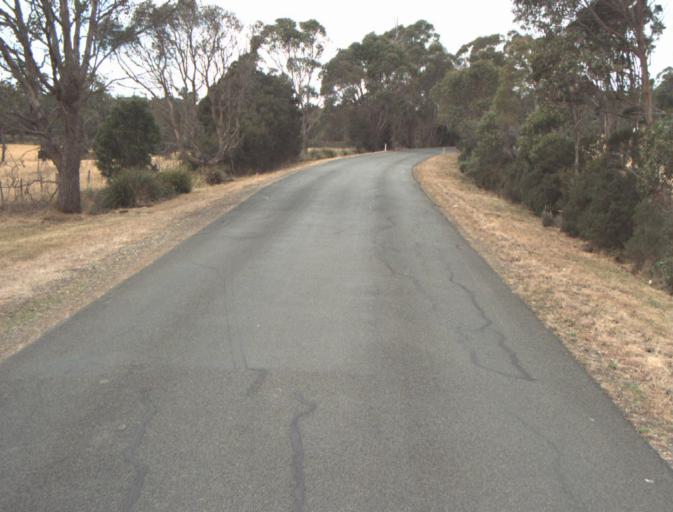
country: AU
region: Tasmania
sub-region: Launceston
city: Mayfield
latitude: -41.2242
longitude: 147.0405
